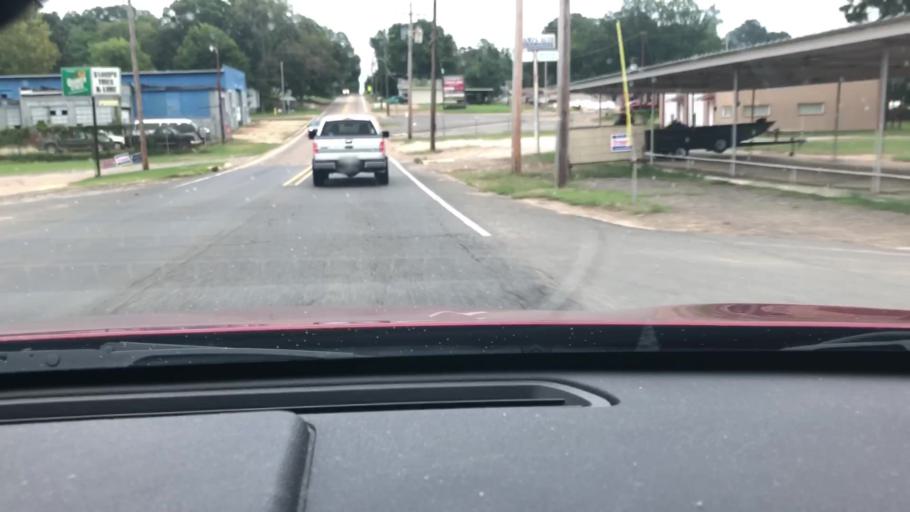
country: US
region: Arkansas
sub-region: Lafayette County
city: Stamps
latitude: 33.3656
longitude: -93.4993
